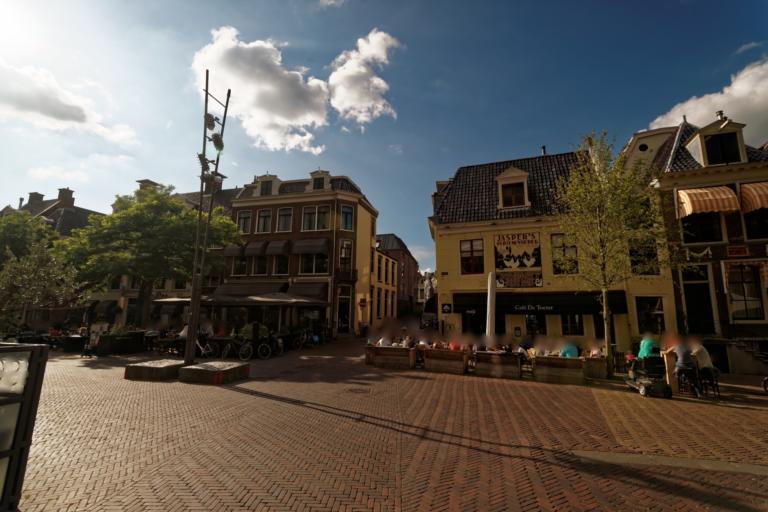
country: NL
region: Friesland
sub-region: Gemeente Leeuwarden
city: Leeuwarden
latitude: 53.2026
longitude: 5.7968
